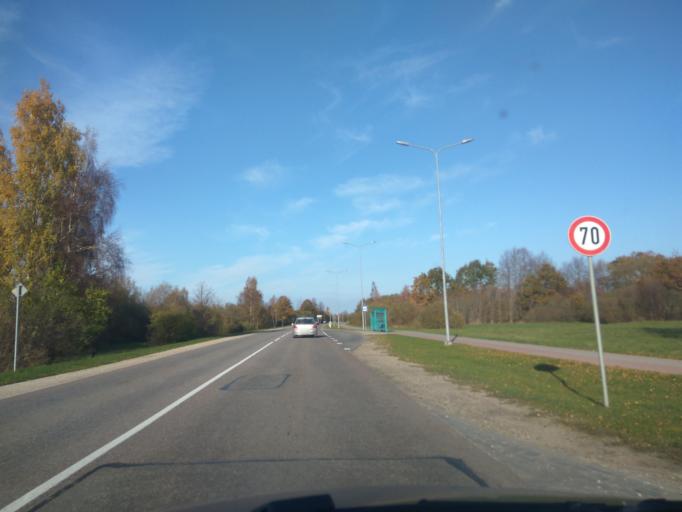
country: LV
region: Ventspils
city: Ventspils
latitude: 57.3601
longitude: 21.5632
